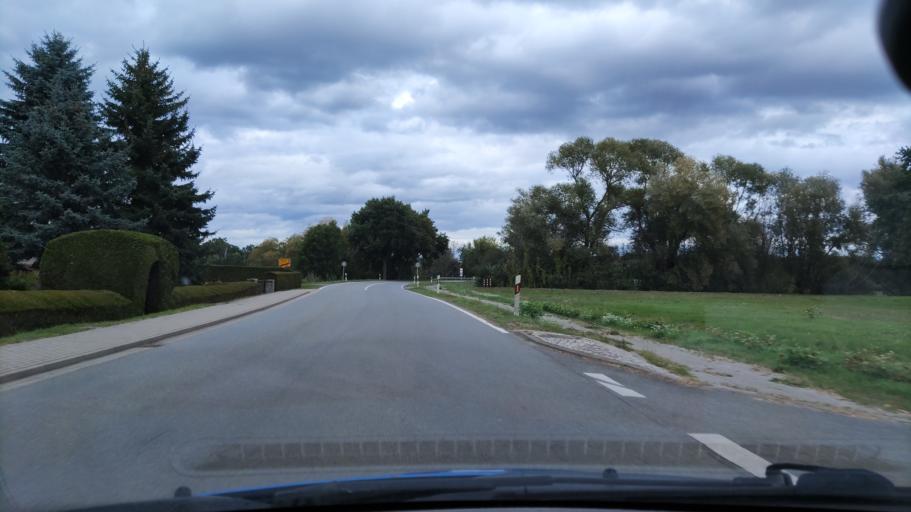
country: DE
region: Lower Saxony
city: Neu Darchau
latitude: 53.2996
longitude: 10.9677
